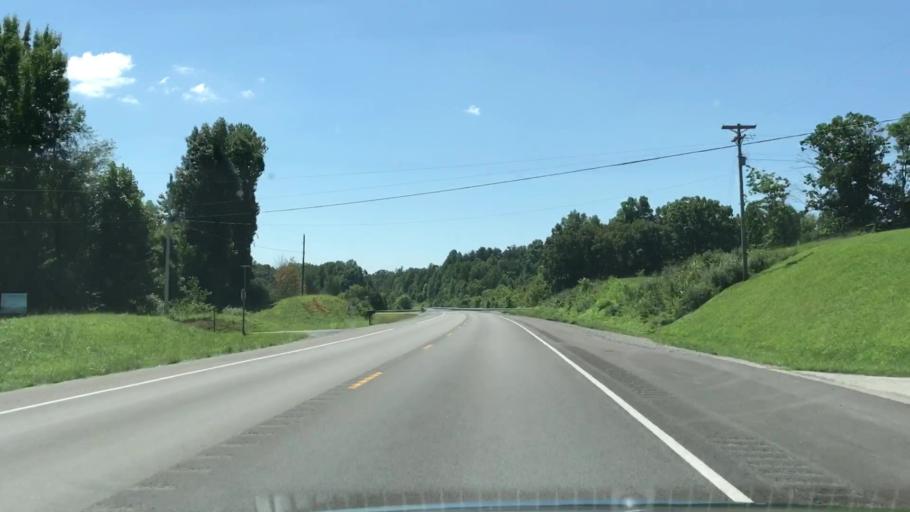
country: US
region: Kentucky
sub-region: Cumberland County
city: Burkesville
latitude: 36.6908
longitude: -85.3741
